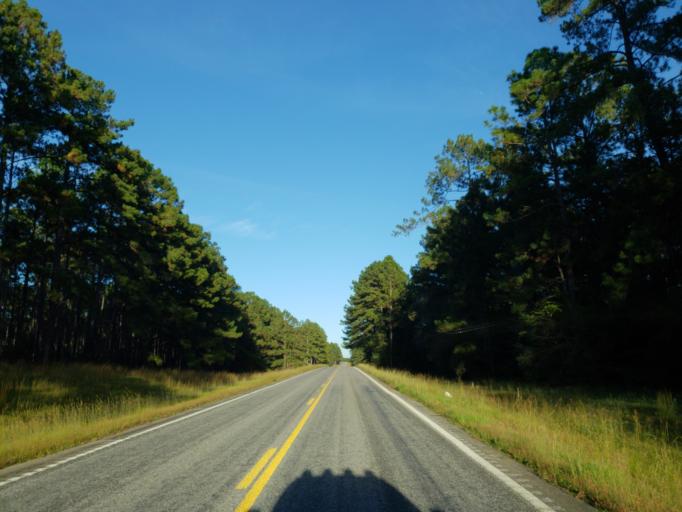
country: US
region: Mississippi
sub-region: Wayne County
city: Belmont
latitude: 31.3995
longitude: -88.6365
